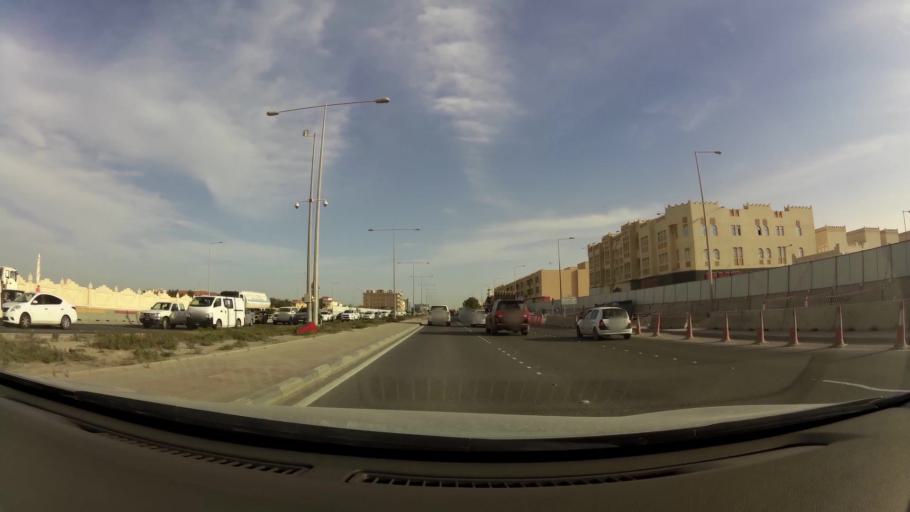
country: QA
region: Al Wakrah
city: Al Wakrah
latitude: 25.1910
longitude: 51.5973
